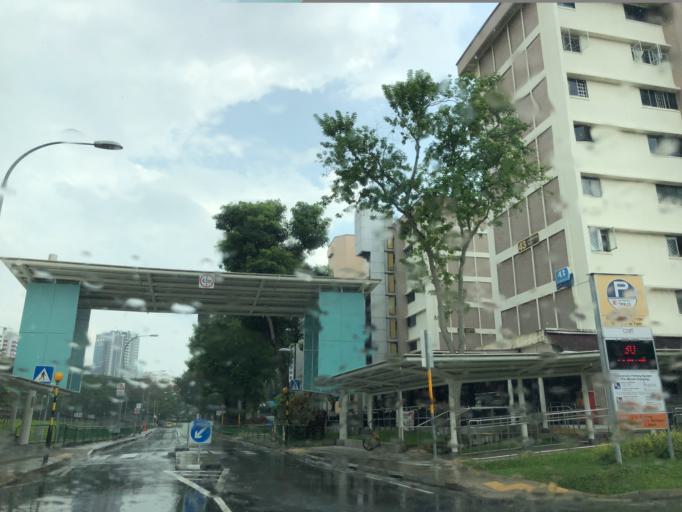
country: SG
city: Singapore
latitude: 1.3155
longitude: 103.8489
